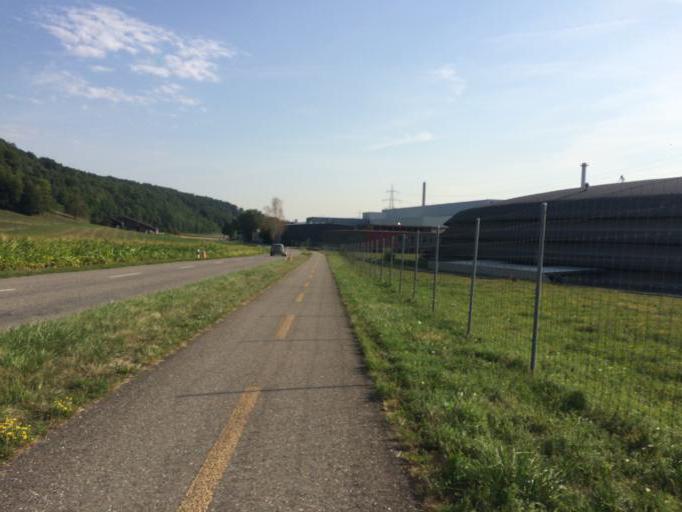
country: CH
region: Aargau
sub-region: Bezirk Brugg
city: Villigen
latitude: 47.5341
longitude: 8.2197
